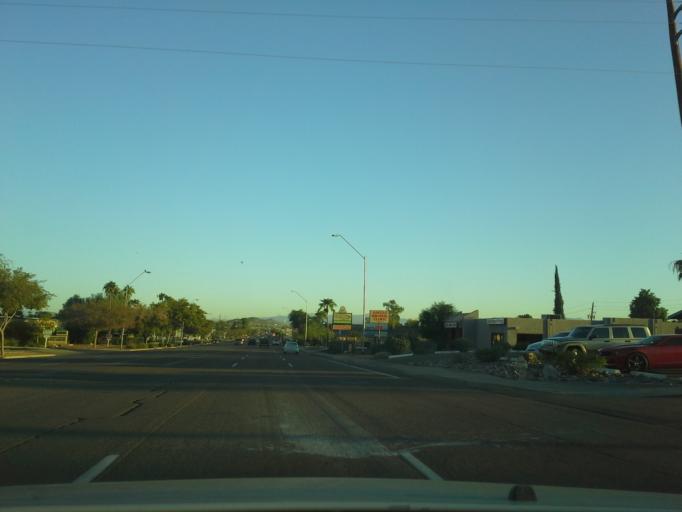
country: US
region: Arizona
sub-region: Maricopa County
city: Paradise Valley
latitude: 33.6202
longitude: -112.0306
